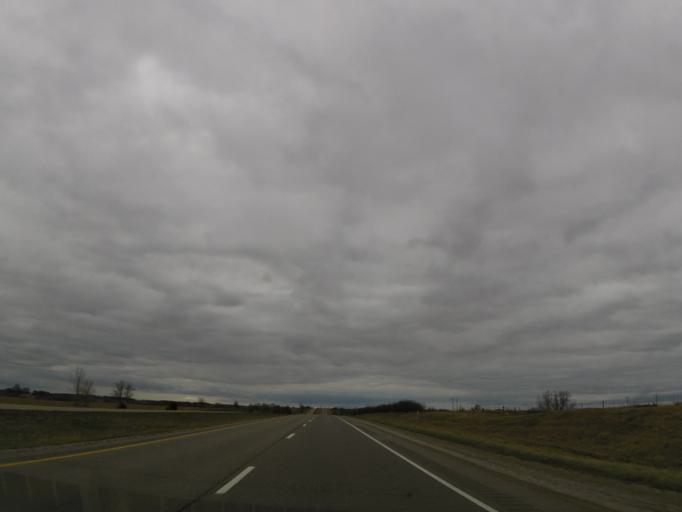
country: US
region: Iowa
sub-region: Washington County
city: Washington
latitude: 41.3708
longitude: -91.5516
